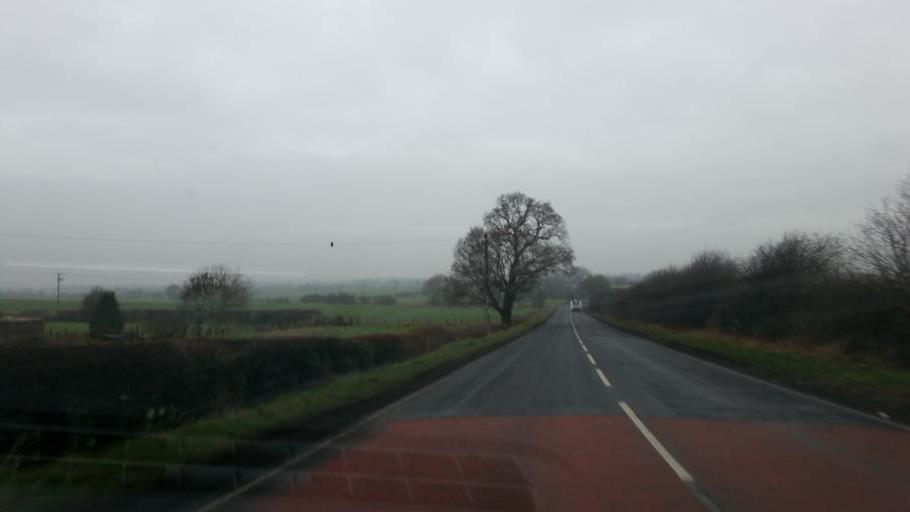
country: GB
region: England
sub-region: City and Borough of Wakefield
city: Badsworth
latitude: 53.6430
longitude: -1.2814
